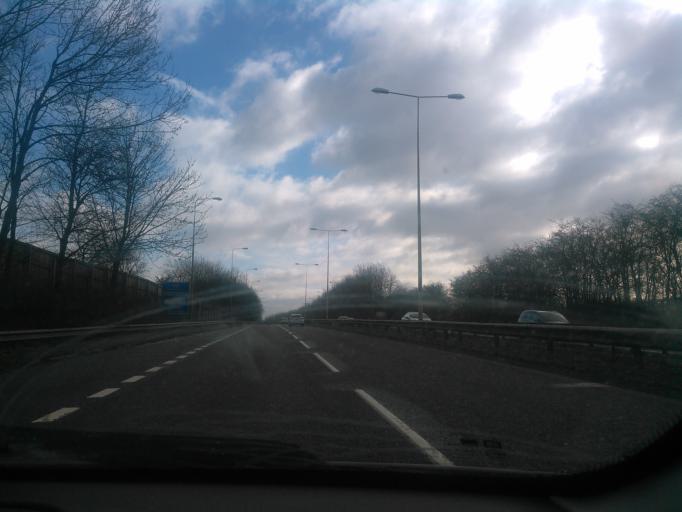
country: GB
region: England
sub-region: Staffordshire
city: Longton
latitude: 52.9649
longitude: -2.0731
